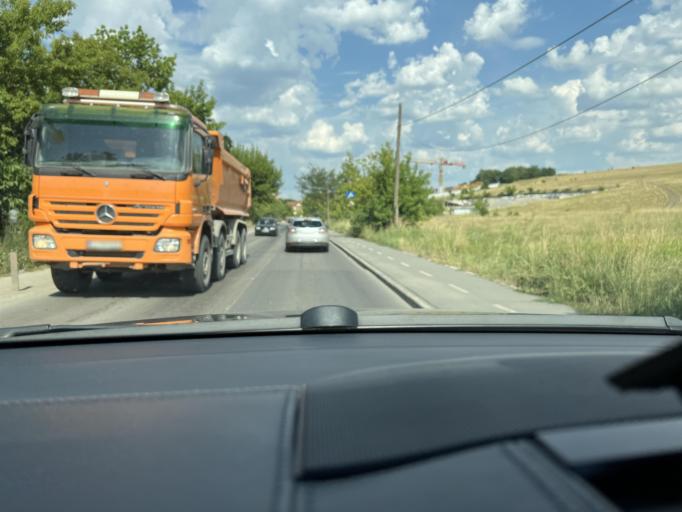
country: RO
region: Cluj
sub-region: Comuna Apahida
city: Dezmir
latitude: 46.7785
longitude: 23.6688
